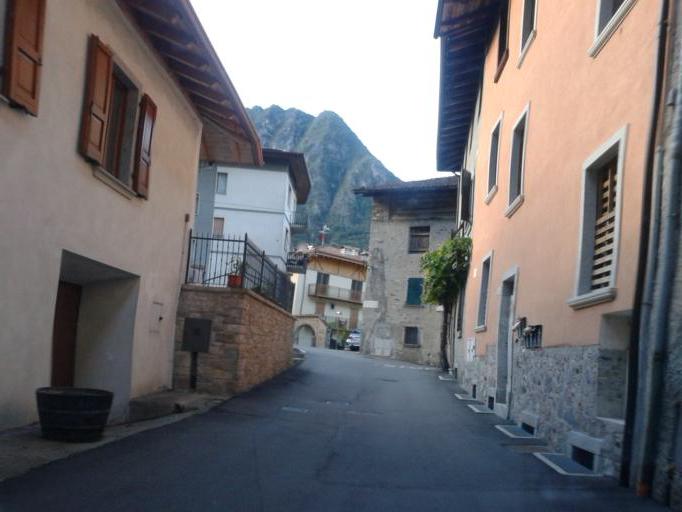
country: IT
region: Trentino-Alto Adige
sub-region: Provincia di Trento
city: Storo
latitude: 45.8512
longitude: 10.5786
